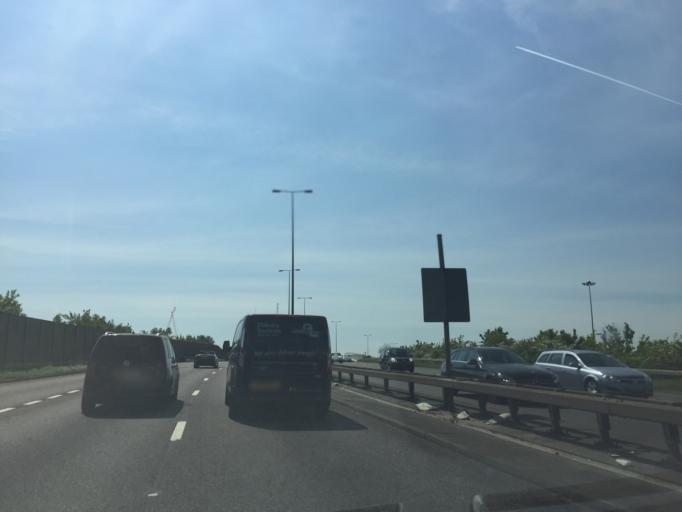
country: GB
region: England
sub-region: Greater London
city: Walthamstow
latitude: 51.5544
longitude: -0.0082
